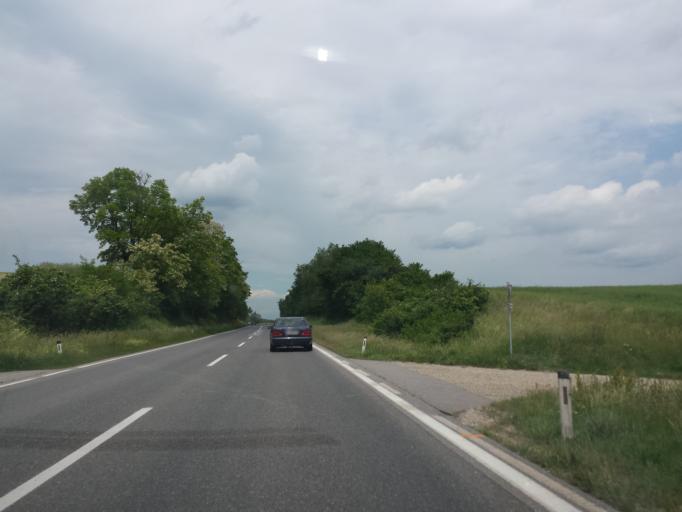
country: AT
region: Lower Austria
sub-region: Politischer Bezirk Mistelbach
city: Wilfersdorf
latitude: 48.6075
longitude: 16.6482
